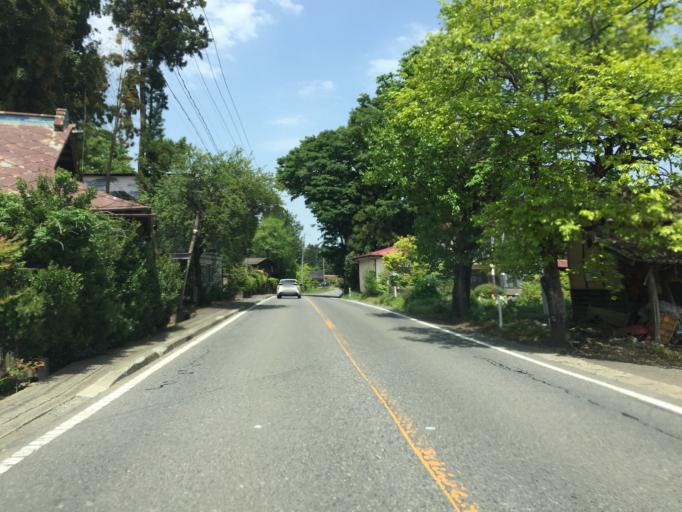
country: JP
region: Fukushima
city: Ishikawa
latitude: 37.1272
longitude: 140.3713
